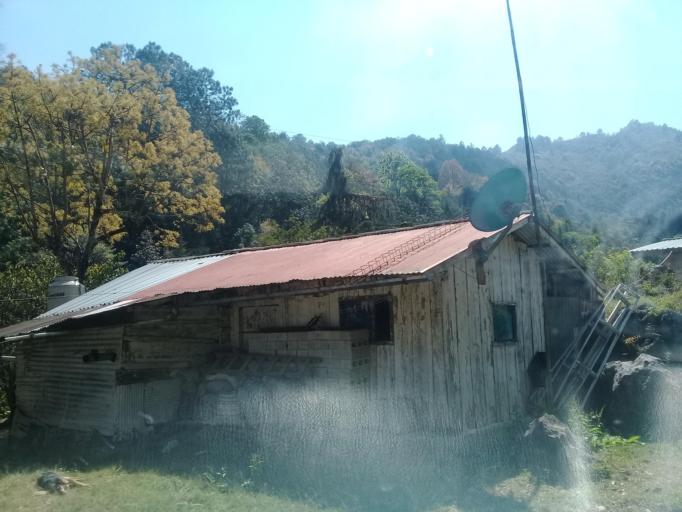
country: MX
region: Veracruz
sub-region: Tlilapan
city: Tonalixco
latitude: 18.7560
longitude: -97.0425
